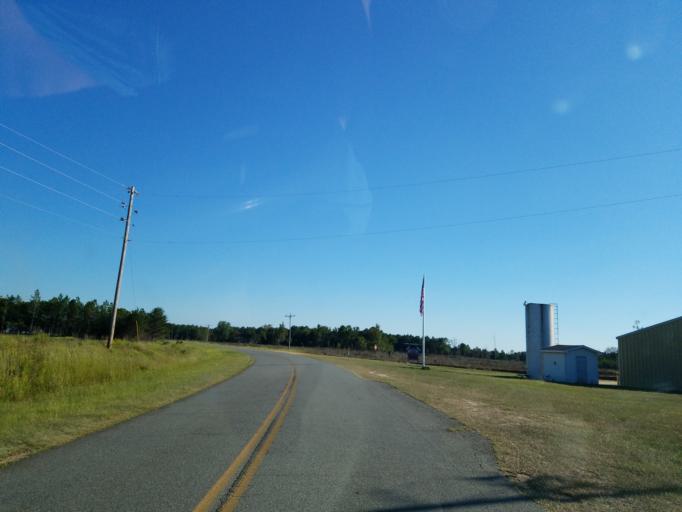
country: US
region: Georgia
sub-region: Dooly County
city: Vienna
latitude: 32.0714
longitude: -83.9560
